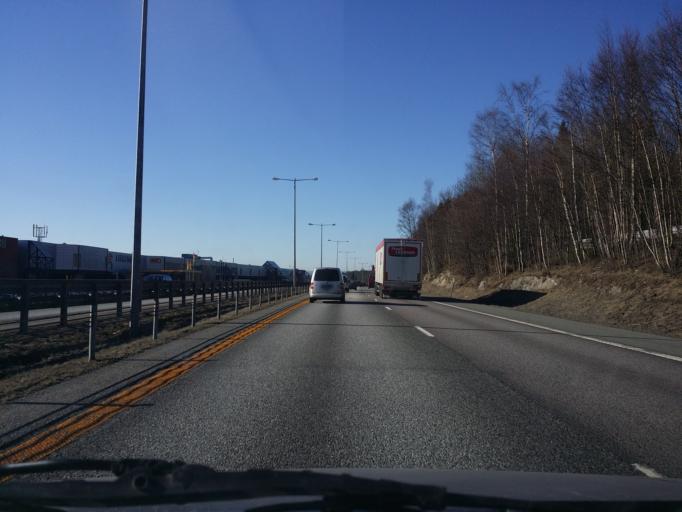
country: NO
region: Buskerud
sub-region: Lier
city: Tranby
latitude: 59.8124
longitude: 10.3061
